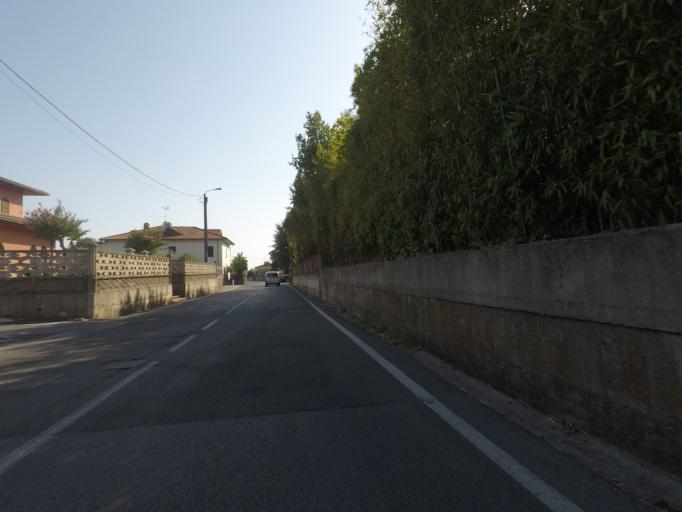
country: IT
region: Liguria
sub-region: Provincia di La Spezia
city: Casano-Dogana-Isola
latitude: 44.0797
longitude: 10.0321
